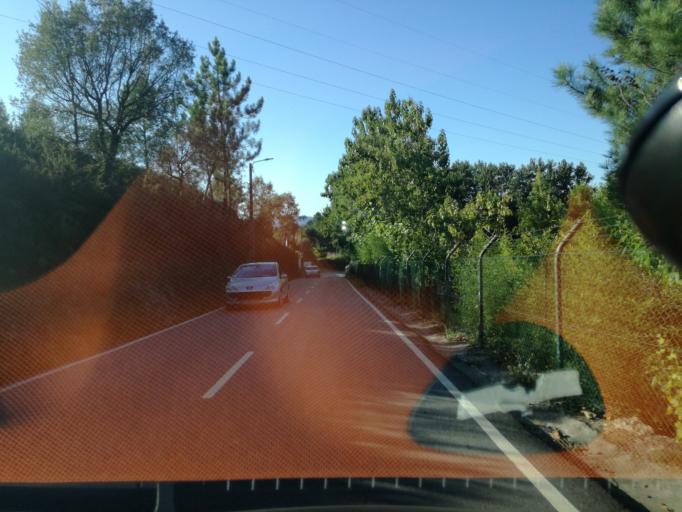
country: PT
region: Porto
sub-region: Santo Tirso
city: Sao Miguel do Couto
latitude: 41.3130
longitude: -8.4631
